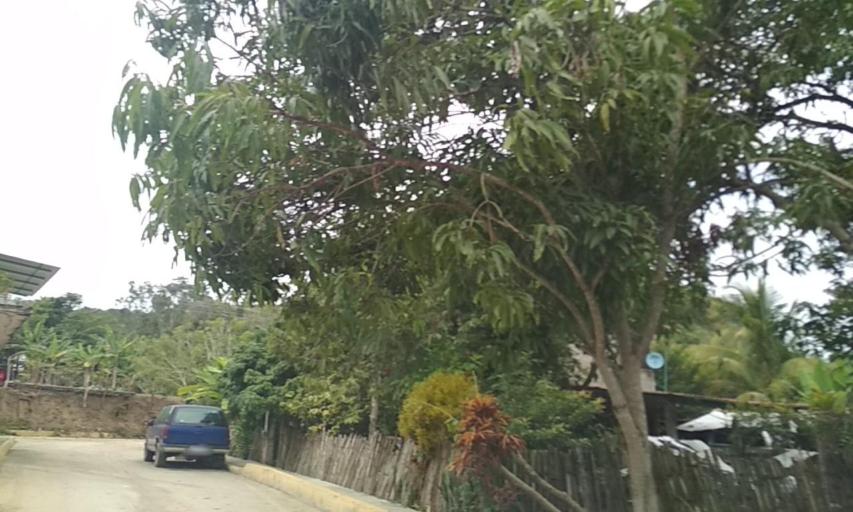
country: MX
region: Veracruz
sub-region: Papantla
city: Residencial Tajin
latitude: 20.6020
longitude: -97.3365
